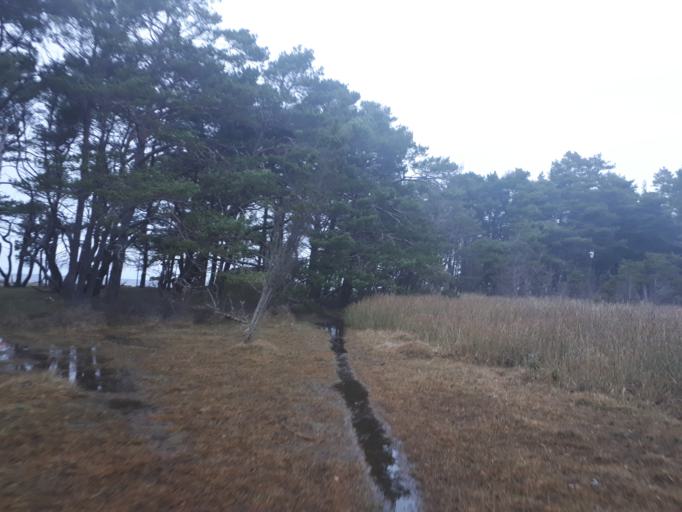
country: SE
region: Gotland
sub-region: Gotland
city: Visby
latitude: 57.6872
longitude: 18.3464
